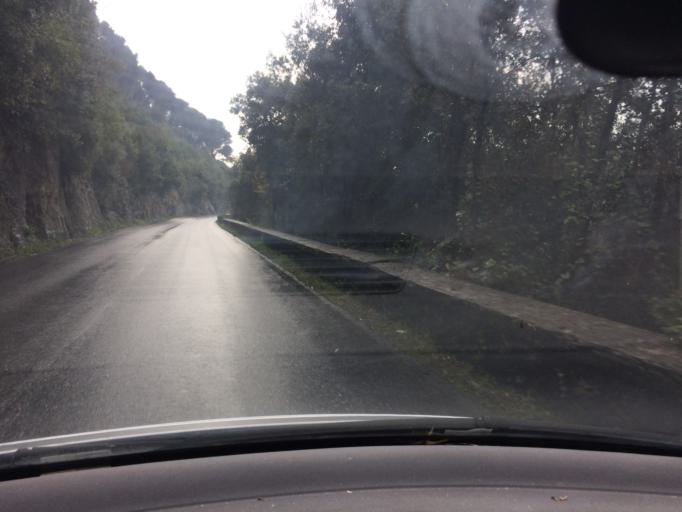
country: IT
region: Tuscany
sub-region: Provincia di Massa-Carrara
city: Massa
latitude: 44.0612
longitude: 10.1185
